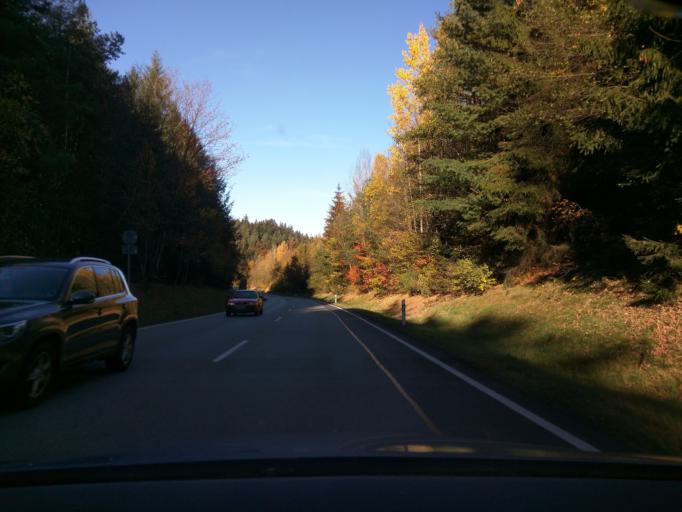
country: DE
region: Bavaria
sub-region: Lower Bavaria
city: Salzweg
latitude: 48.6023
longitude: 13.4782
